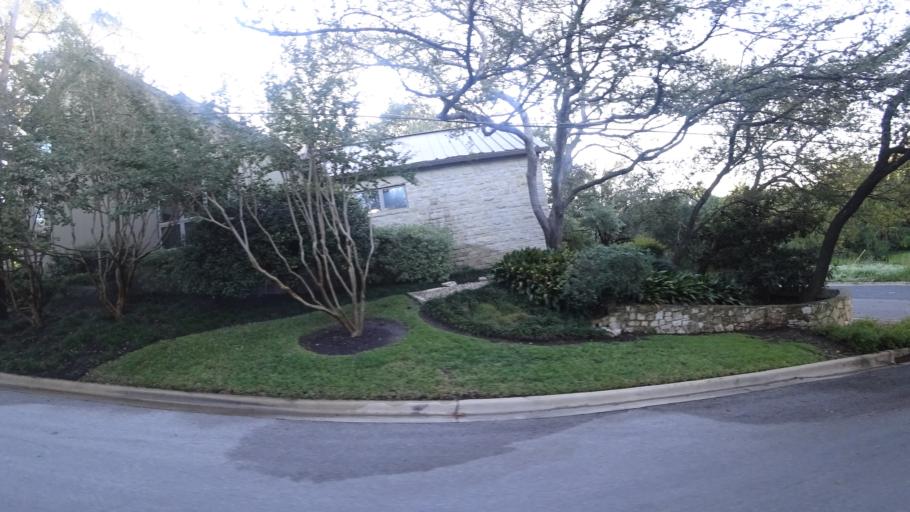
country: US
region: Texas
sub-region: Travis County
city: West Lake Hills
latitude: 30.2997
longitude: -97.7813
